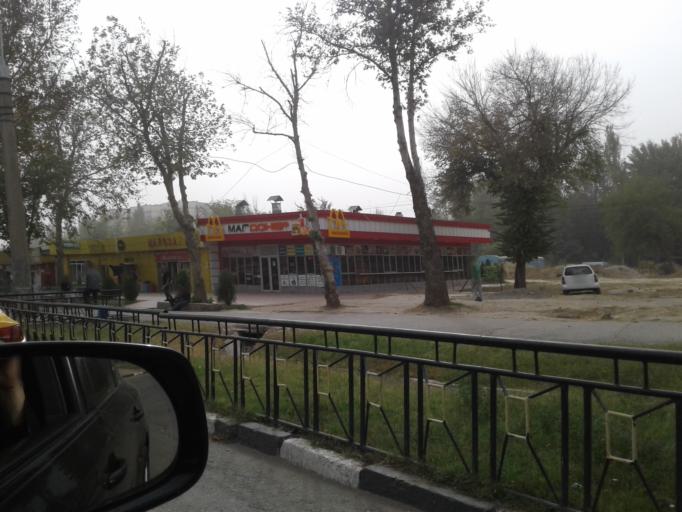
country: TJ
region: Dushanbe
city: Dushanbe
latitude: 38.5725
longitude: 68.7546
